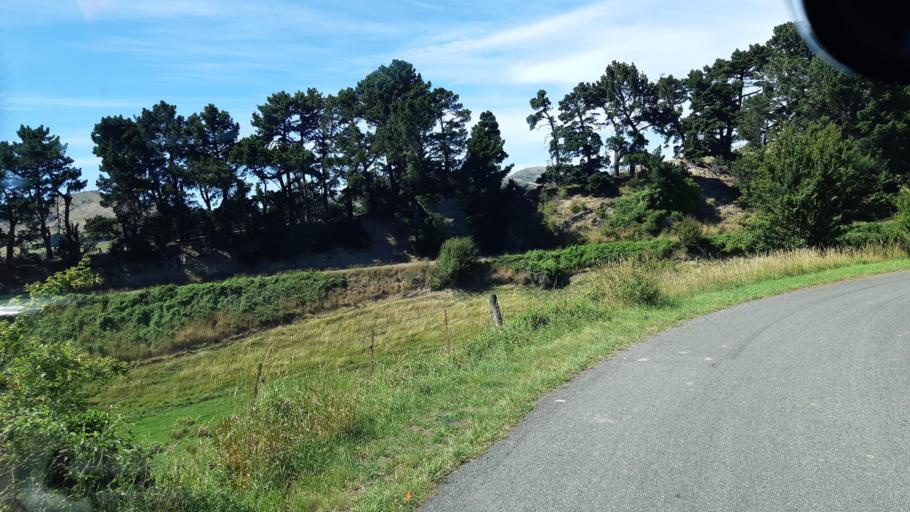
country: NZ
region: Marlborough
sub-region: Marlborough District
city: Blenheim
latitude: -41.8280
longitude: 174.1184
